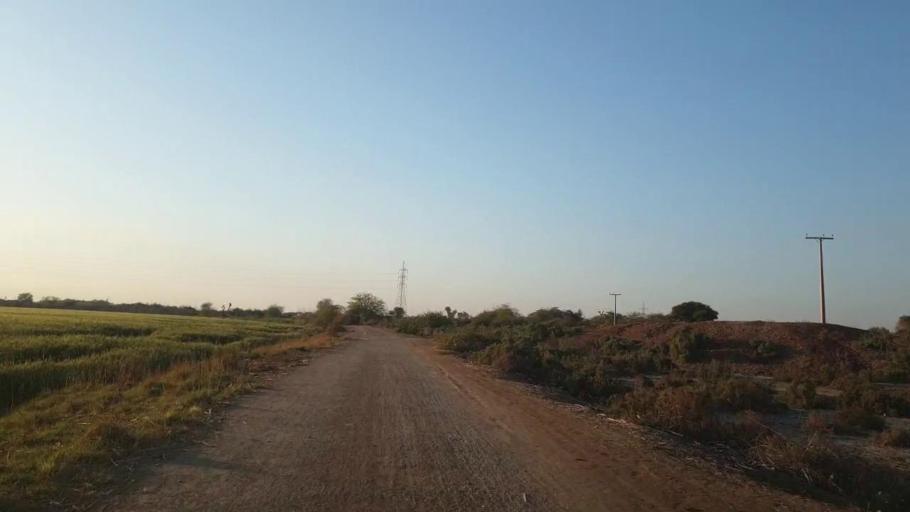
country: PK
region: Sindh
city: Mirpur Khas
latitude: 25.7013
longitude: 69.0427
